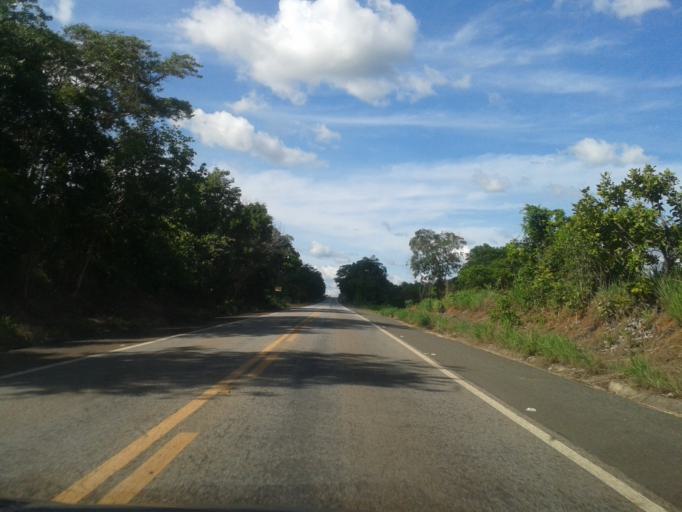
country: BR
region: Goias
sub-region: Mozarlandia
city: Mozarlandia
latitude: -14.9762
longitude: -50.5807
